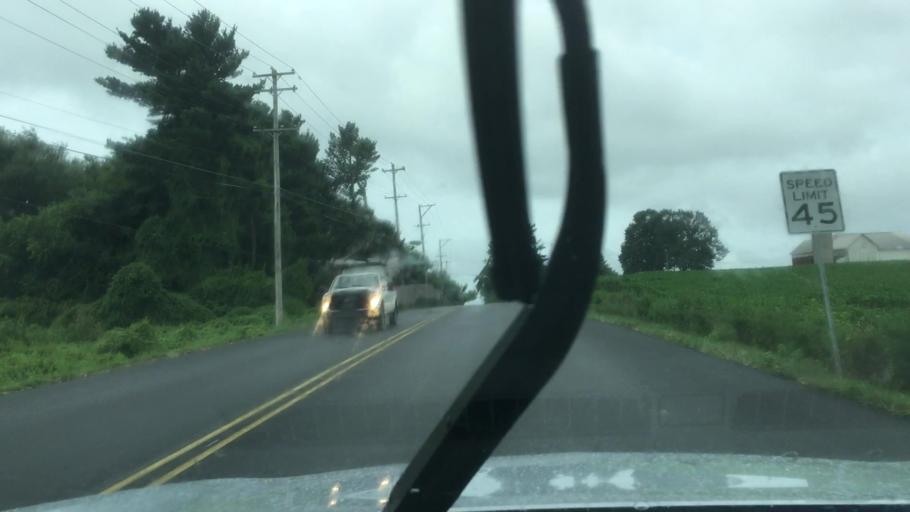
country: US
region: Pennsylvania
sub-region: Chester County
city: West Grove
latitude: 39.8637
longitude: -75.8515
